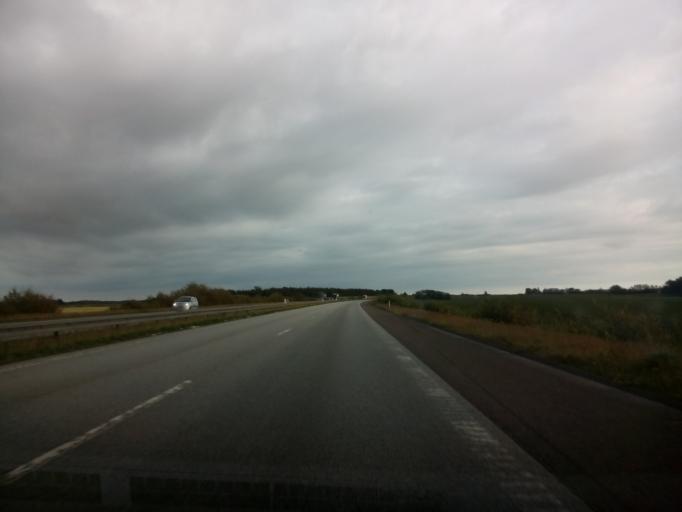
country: DK
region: North Denmark
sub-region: Hjorring Kommune
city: Hjorring
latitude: 57.4064
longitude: 10.0298
